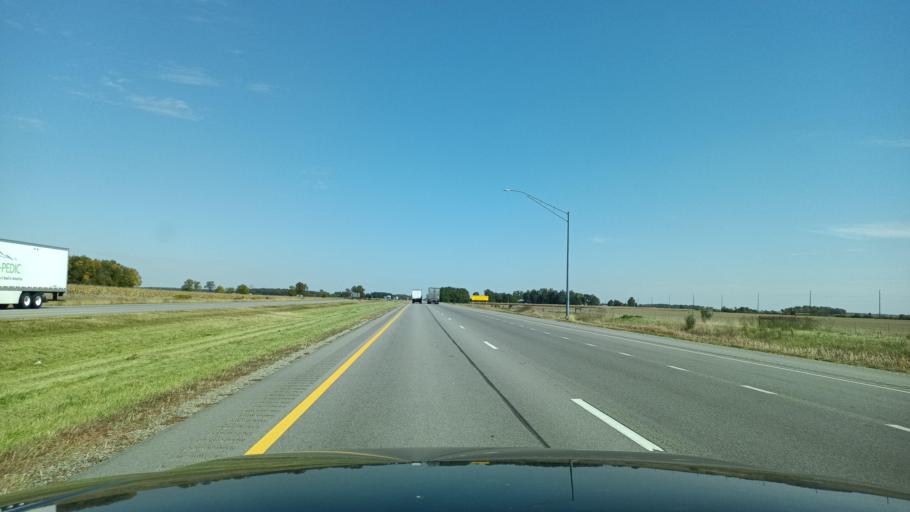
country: US
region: Ohio
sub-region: Defiance County
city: Defiance
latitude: 41.3151
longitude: -84.3172
